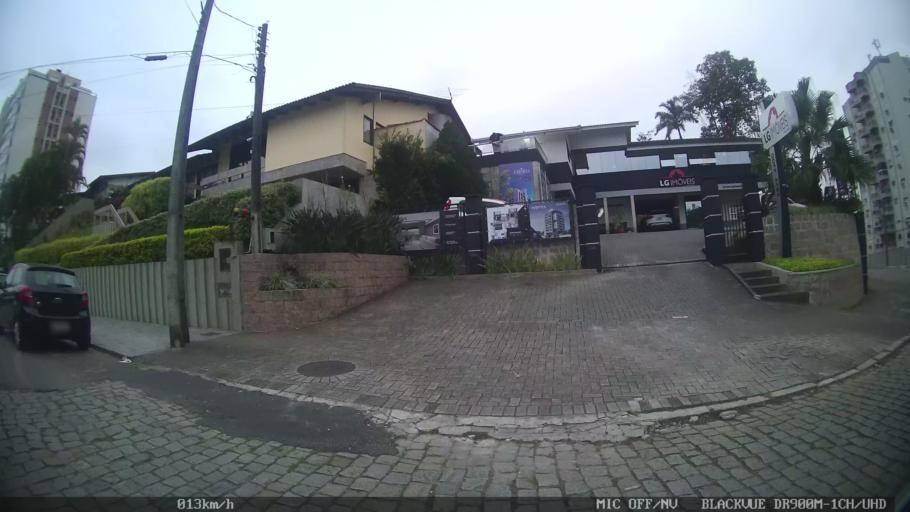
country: BR
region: Santa Catarina
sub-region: Joinville
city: Joinville
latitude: -26.3069
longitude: -48.8592
